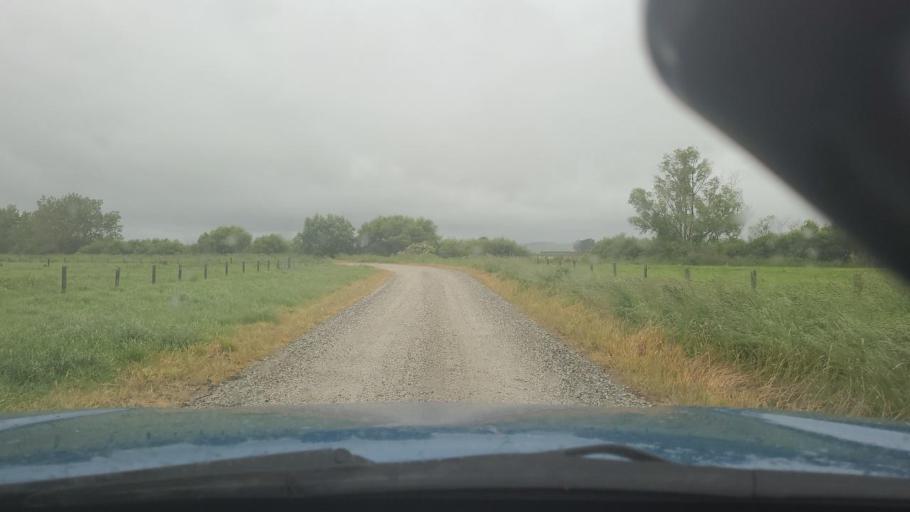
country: NZ
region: Southland
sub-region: Gore District
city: Gore
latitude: -46.3962
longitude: 168.7687
